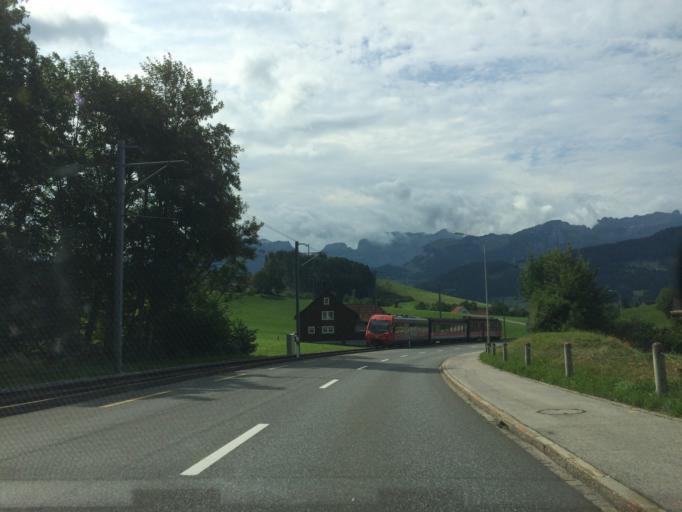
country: CH
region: Appenzell Innerrhoden
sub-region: Appenzell Inner Rhodes
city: Appenzell
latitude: 47.3428
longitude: 9.4295
